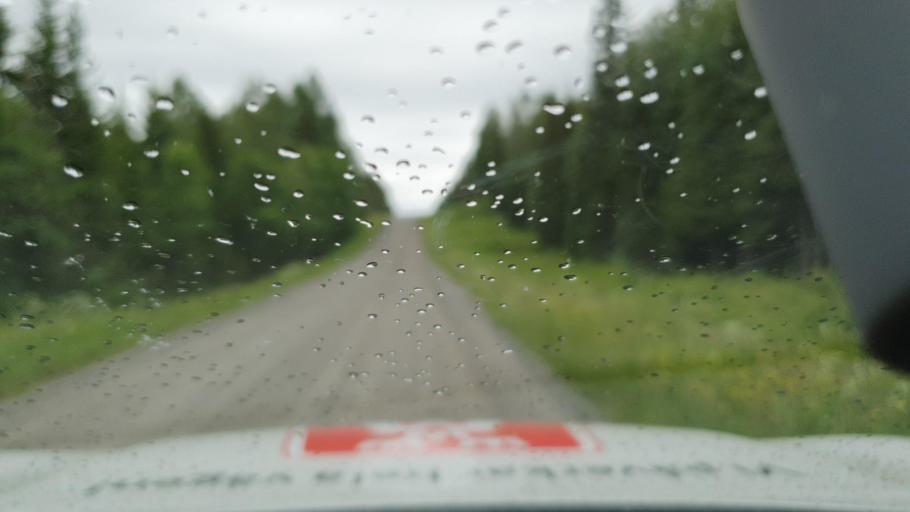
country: SE
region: Vaesterbotten
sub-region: Nordmalings Kommun
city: Nordmaling
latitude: 63.7561
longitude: 19.4920
